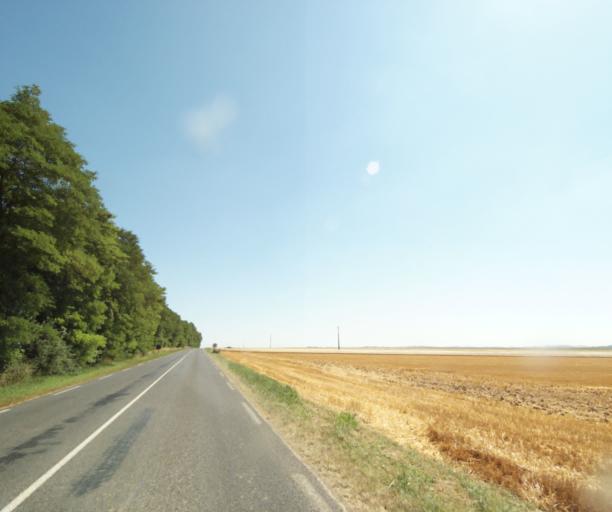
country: FR
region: Ile-de-France
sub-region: Departement de Seine-et-Marne
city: La Chapelle-la-Reine
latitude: 48.3018
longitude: 2.5736
